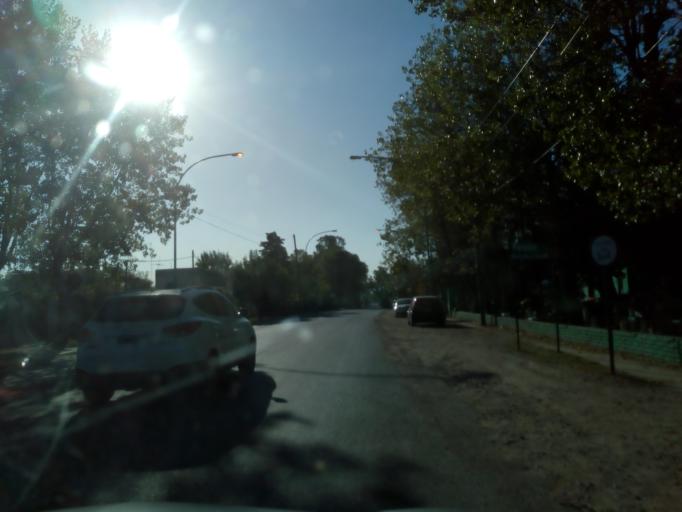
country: AR
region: Buenos Aires
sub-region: Partido de Ensenada
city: Ensenada
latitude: -34.8221
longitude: -57.9646
